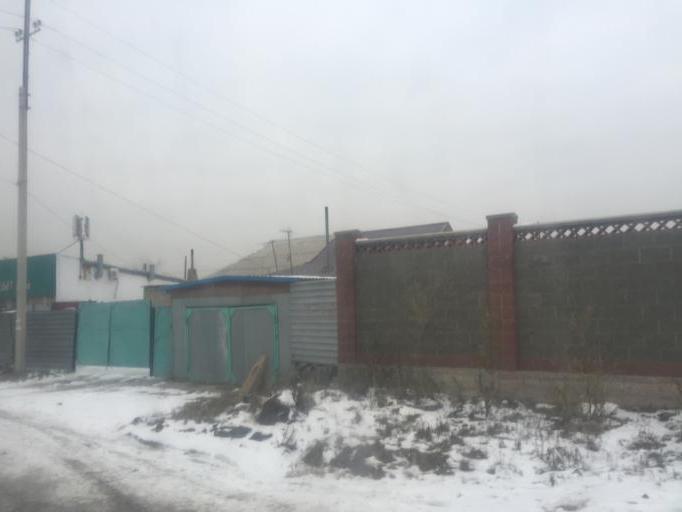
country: KZ
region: Astana Qalasy
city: Astana
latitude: 51.2050
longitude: 71.4133
